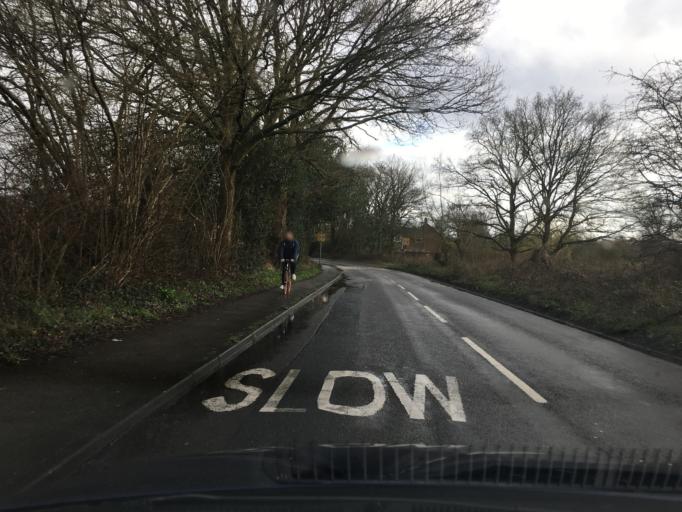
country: GB
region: England
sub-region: Bracknell Forest
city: Sandhurst
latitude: 51.3403
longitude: -0.8014
